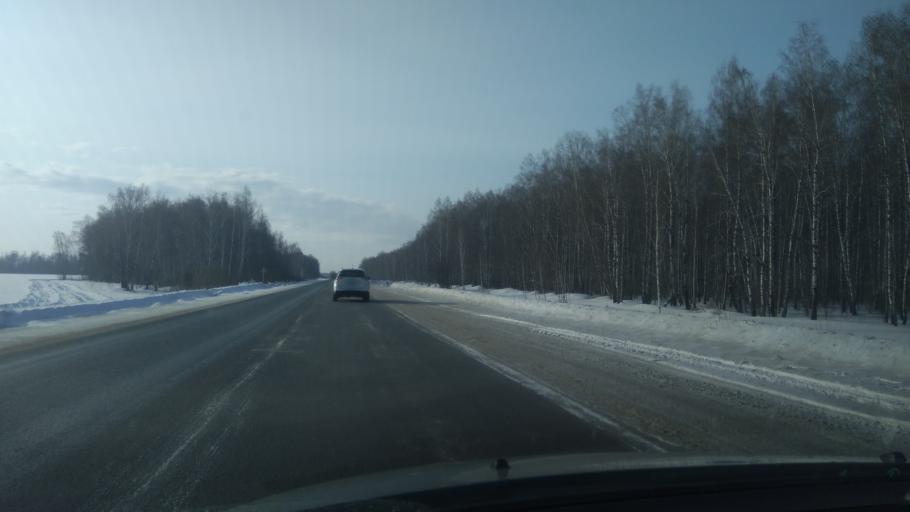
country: RU
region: Sverdlovsk
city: Bogdanovich
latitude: 56.8069
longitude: 62.0320
